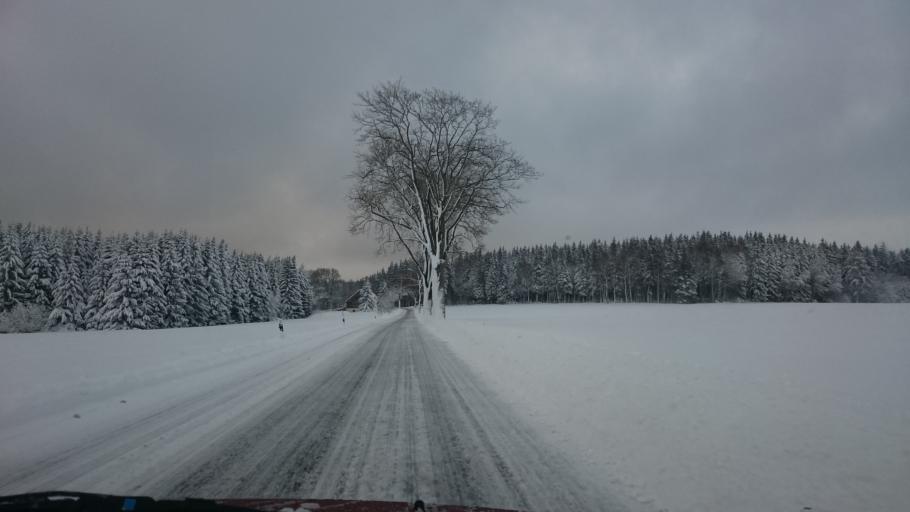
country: DE
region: Saxony
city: Elterlein
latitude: 50.5869
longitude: 12.8826
